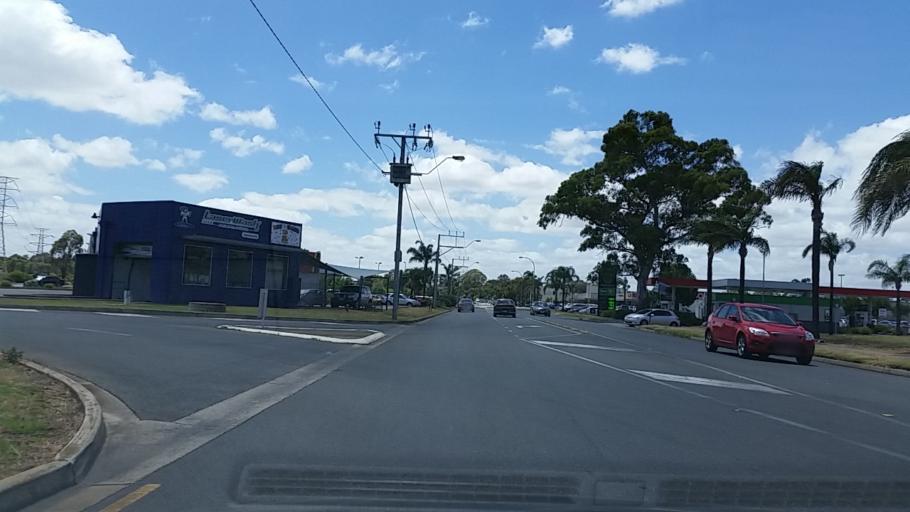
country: AU
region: South Australia
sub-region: Salisbury
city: Salisbury
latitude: -34.7680
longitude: 138.6216
